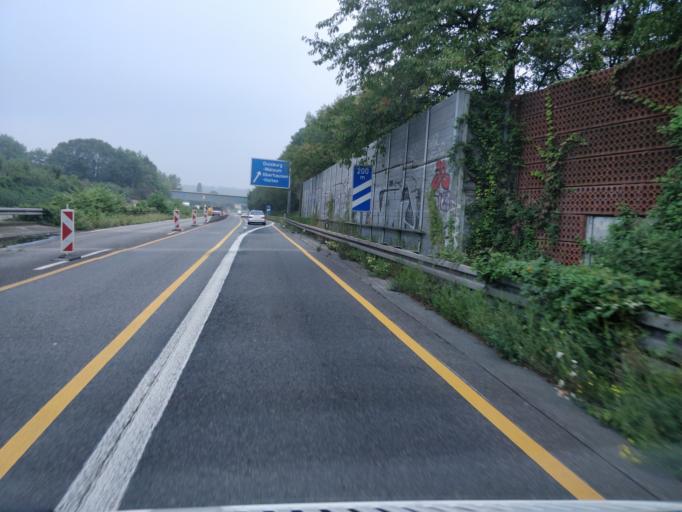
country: DE
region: North Rhine-Westphalia
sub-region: Regierungsbezirk Dusseldorf
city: Dinslaken
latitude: 51.5226
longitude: 6.7600
